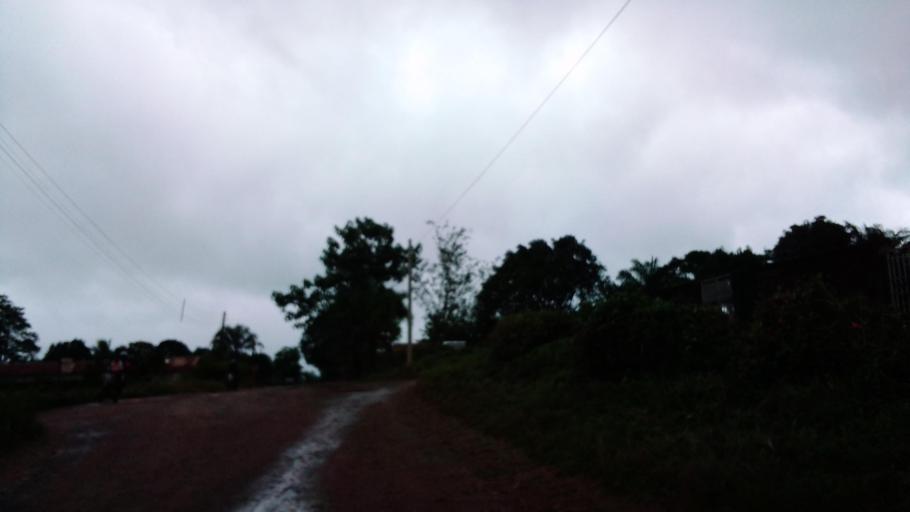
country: SL
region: Eastern Province
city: Kenema
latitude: 7.8491
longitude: -11.2049
